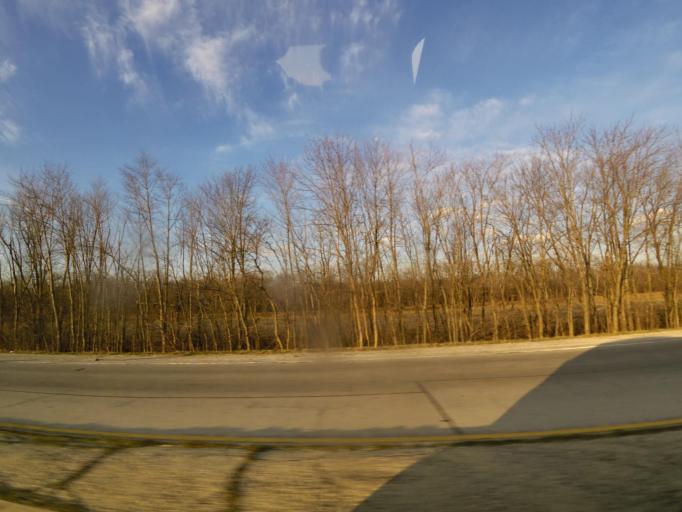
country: US
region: Illinois
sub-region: Fayette County
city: Vandalia
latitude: 38.9574
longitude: -89.0849
